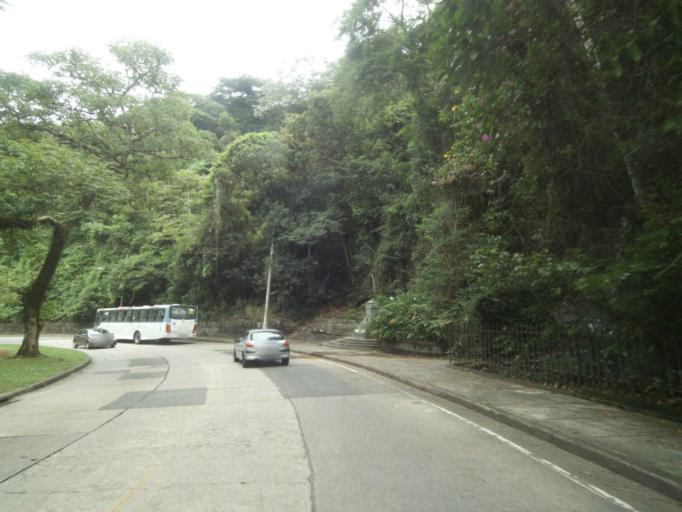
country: BR
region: Rio de Janeiro
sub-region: Rio De Janeiro
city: Rio de Janeiro
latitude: -22.9582
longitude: -43.2655
